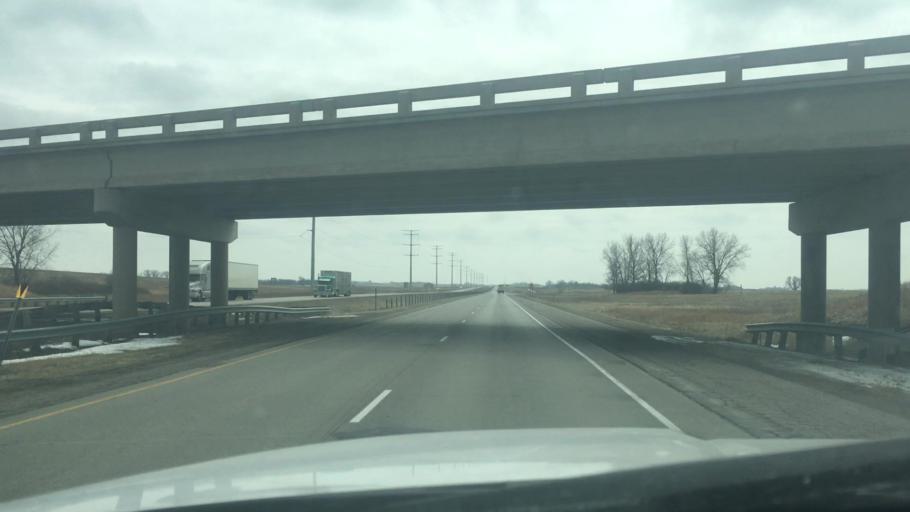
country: US
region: Minnesota
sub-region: Clay County
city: Barnesville
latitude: 46.5587
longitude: -96.3168
